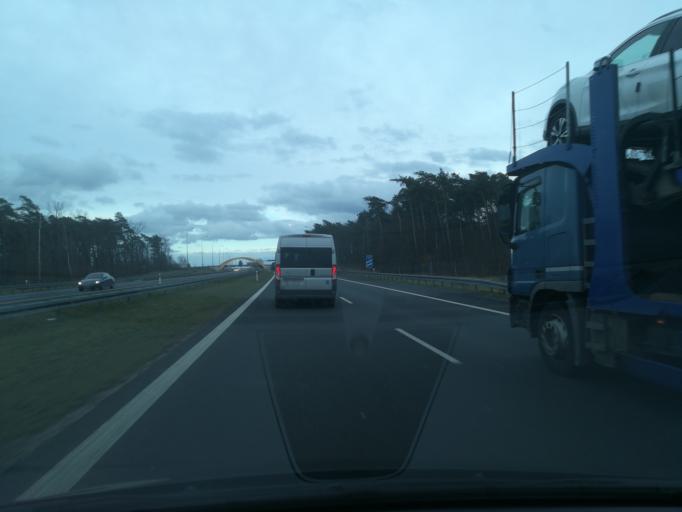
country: PL
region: Lodz Voivodeship
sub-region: Powiat kutnowski
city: Strzelce
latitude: 52.2945
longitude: 19.3820
